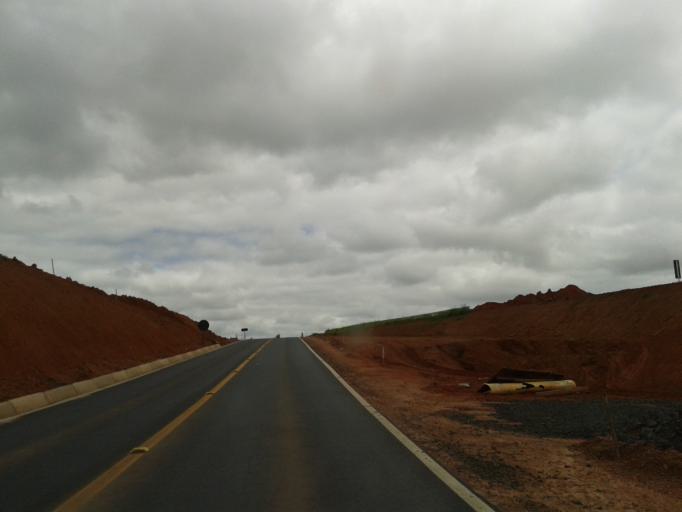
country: BR
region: Minas Gerais
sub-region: Uberlandia
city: Uberlandia
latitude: -19.2748
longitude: -48.1255
